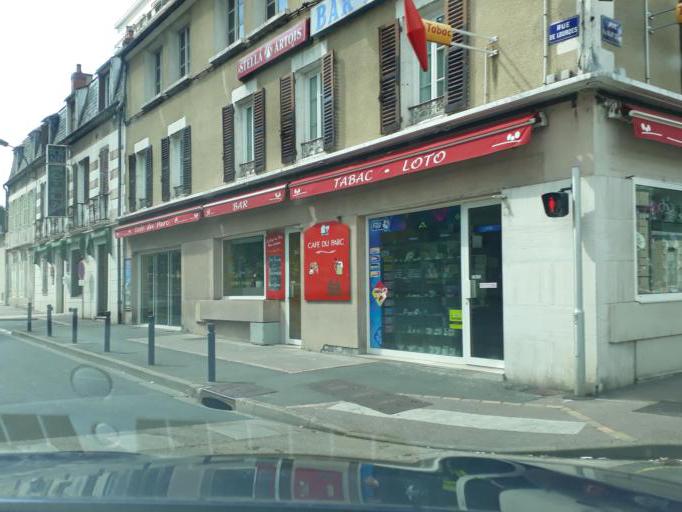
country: FR
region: Bourgogne
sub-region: Departement de la Nievre
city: Nevers
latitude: 46.9914
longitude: 3.1572
